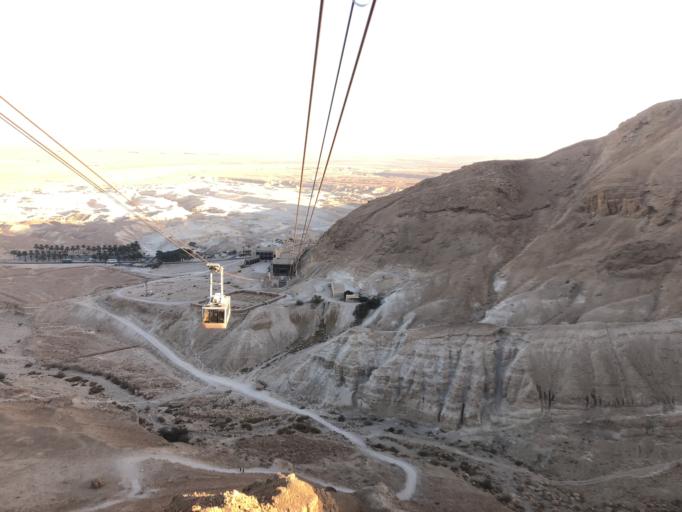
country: IL
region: Southern District
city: `En Boqeq
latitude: 31.3151
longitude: 35.3577
